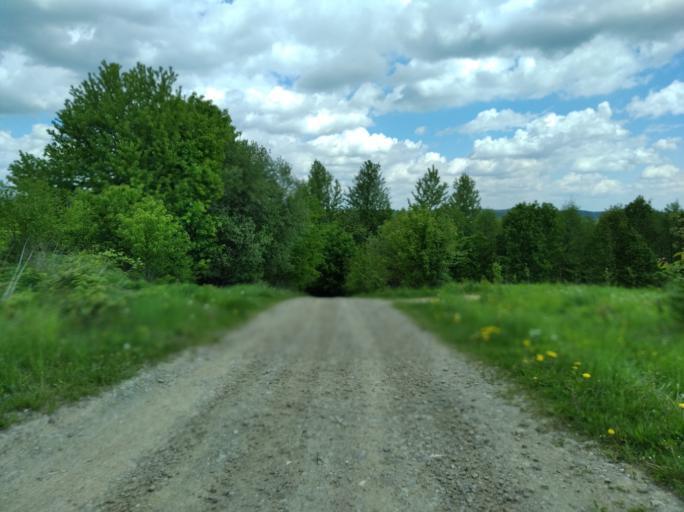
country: PL
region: Subcarpathian Voivodeship
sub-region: Powiat strzyzowski
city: Frysztak
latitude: 49.8327
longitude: 21.5512
